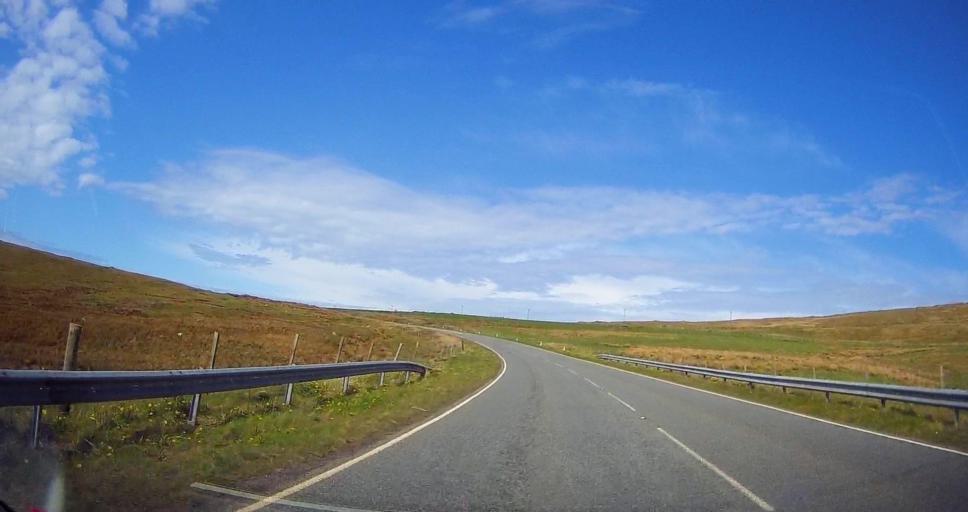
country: GB
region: Scotland
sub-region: Shetland Islands
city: Sandwick
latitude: 60.0104
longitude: -1.2575
